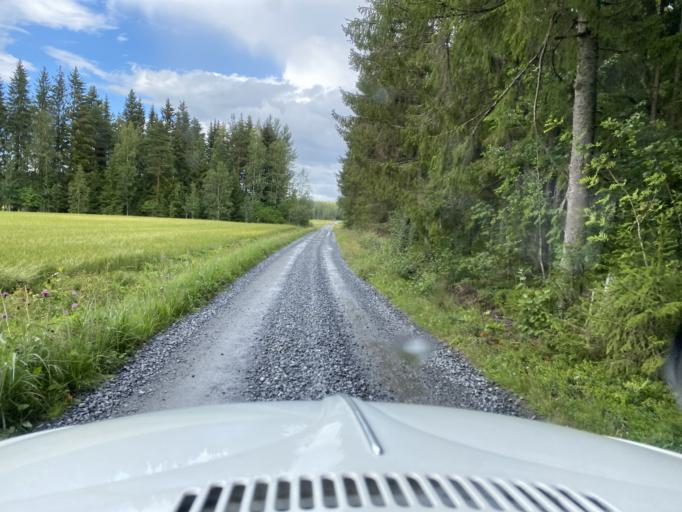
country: FI
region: Pirkanmaa
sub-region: Lounais-Pirkanmaa
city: Punkalaidun
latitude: 61.1305
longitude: 23.0659
